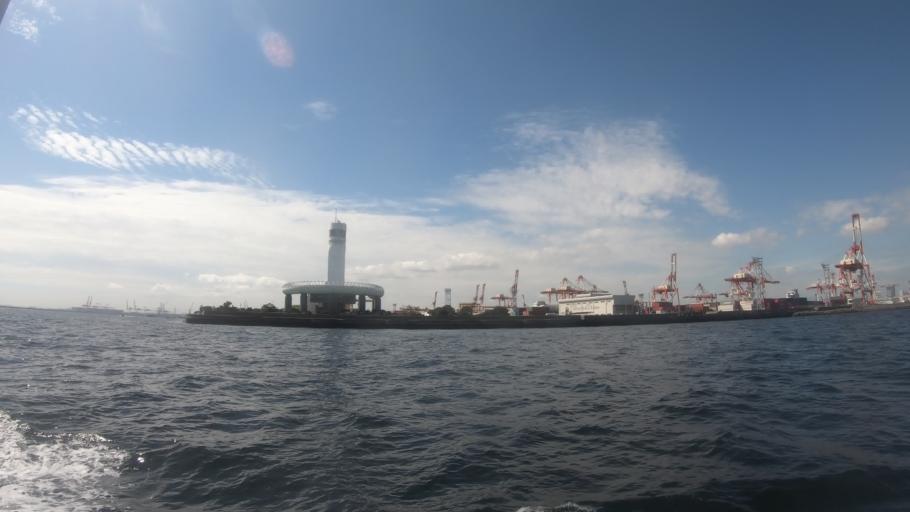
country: JP
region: Kanagawa
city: Yokohama
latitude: 35.4408
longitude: 139.6911
